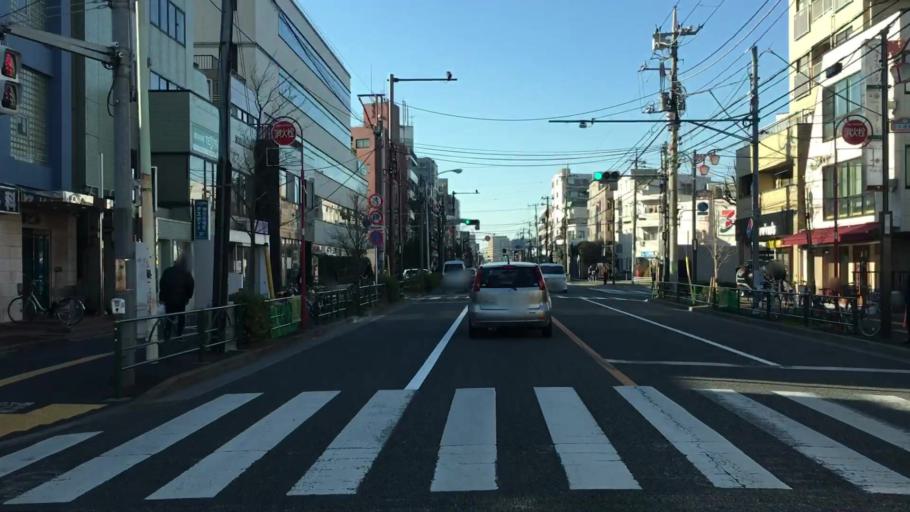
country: JP
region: Tokyo
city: Tokyo
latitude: 35.6797
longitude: 139.6369
